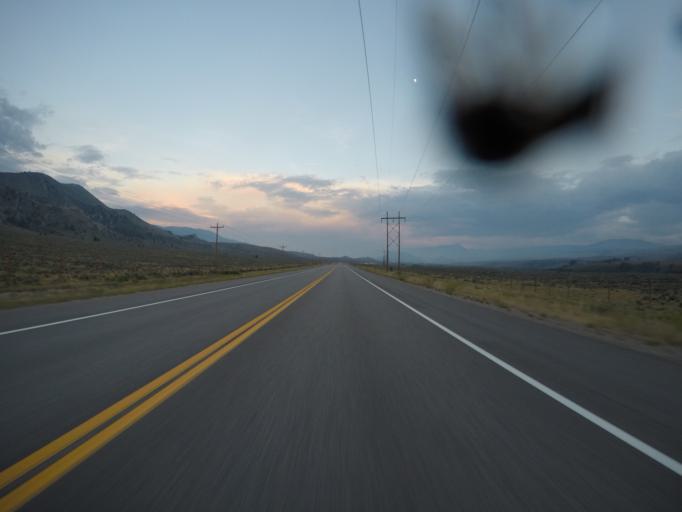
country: US
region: Colorado
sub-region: Grand County
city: Kremmling
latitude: 39.9859
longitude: -106.3581
